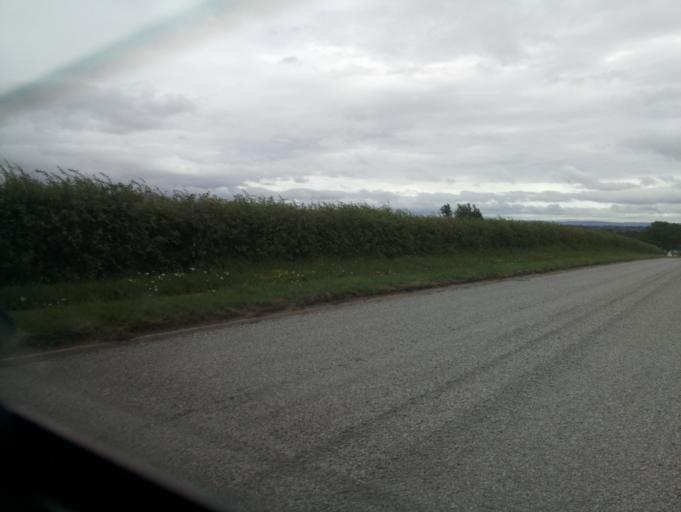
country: GB
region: England
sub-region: Worcestershire
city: Upton upon Severn
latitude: 52.0860
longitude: -2.2029
